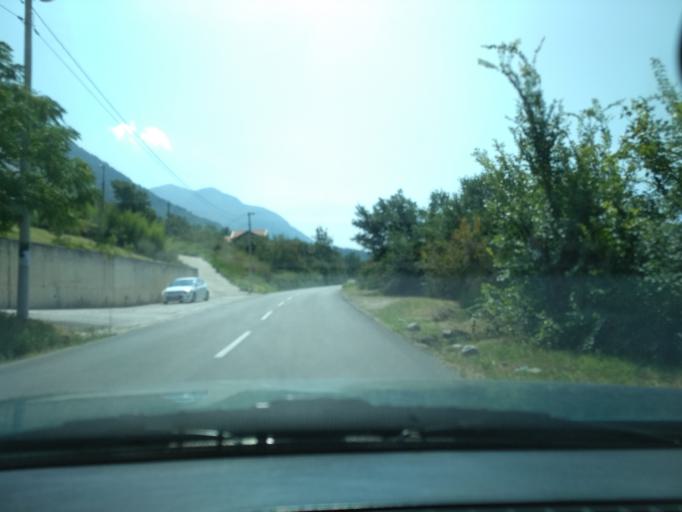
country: ME
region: Kotor
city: Kotor
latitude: 42.3940
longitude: 18.7552
